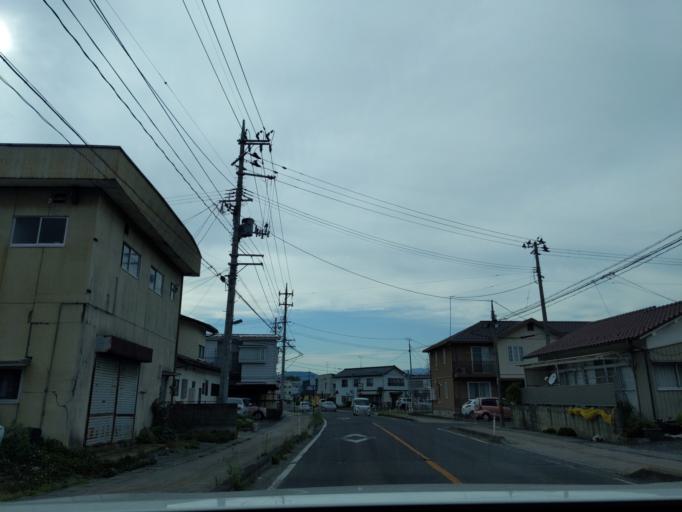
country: JP
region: Fukushima
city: Koriyama
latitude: 37.4104
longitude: 140.3362
